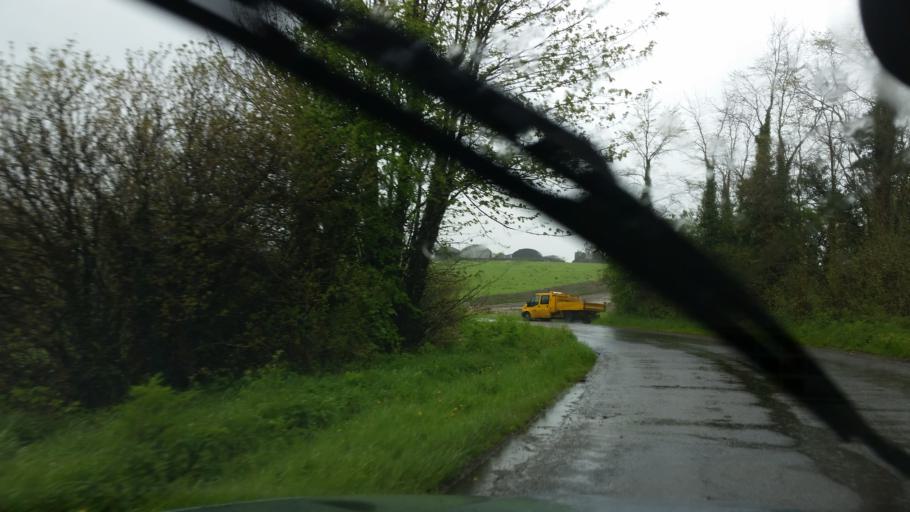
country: GB
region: Northern Ireland
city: Fivemiletown
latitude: 54.3648
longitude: -7.3091
